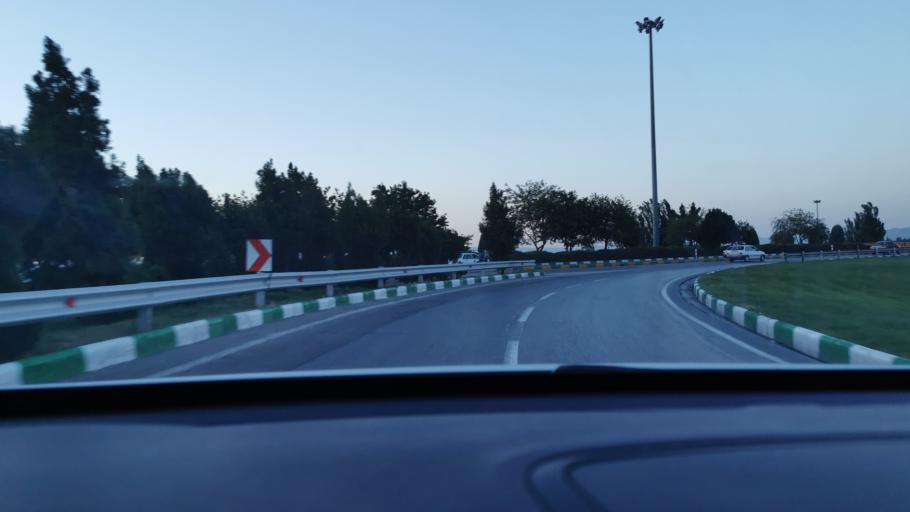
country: IR
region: Razavi Khorasan
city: Mashhad
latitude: 36.3445
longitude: 59.5461
